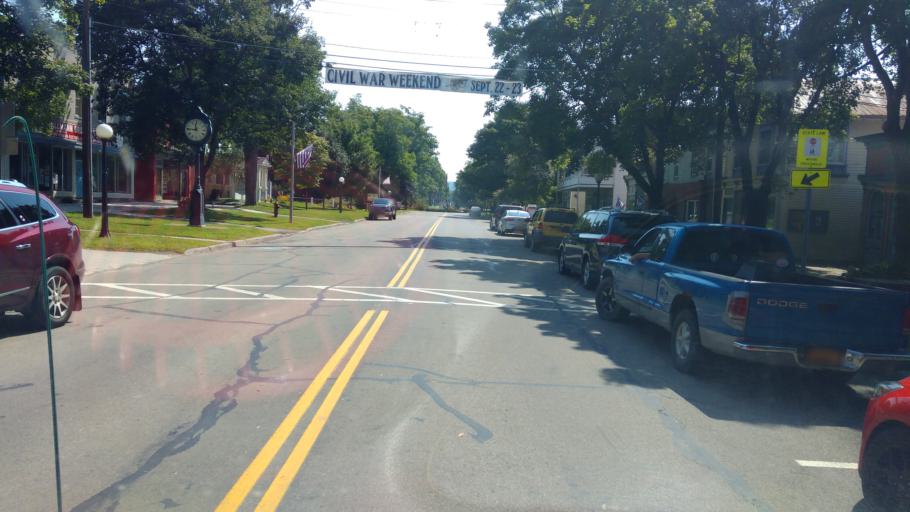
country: US
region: New York
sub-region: Allegany County
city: Belmont
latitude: 42.3068
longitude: -78.0184
